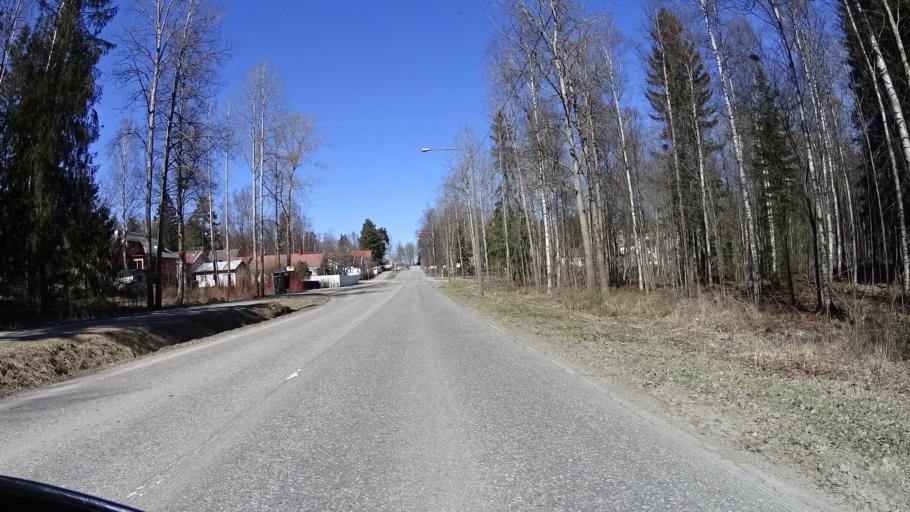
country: FI
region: Uusimaa
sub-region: Helsinki
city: Kilo
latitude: 60.2438
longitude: 24.8086
